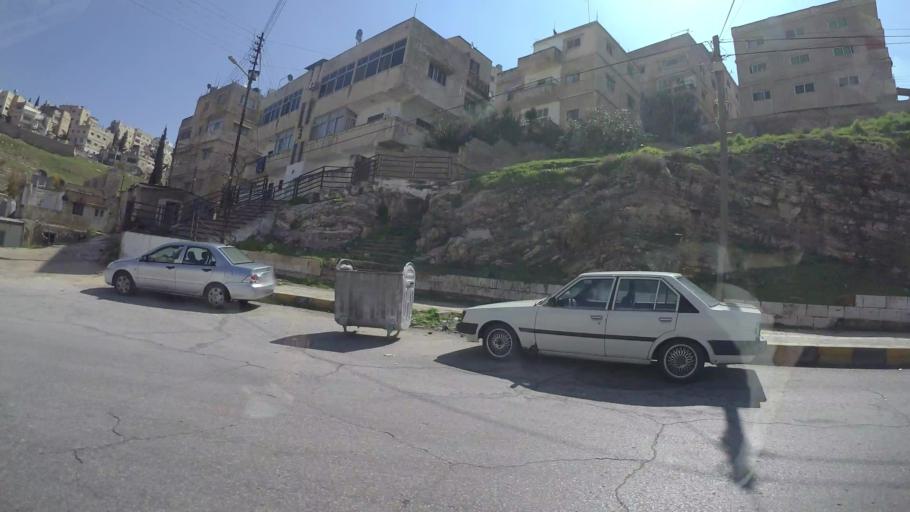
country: JO
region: Amman
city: Amman
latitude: 31.9789
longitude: 35.9782
